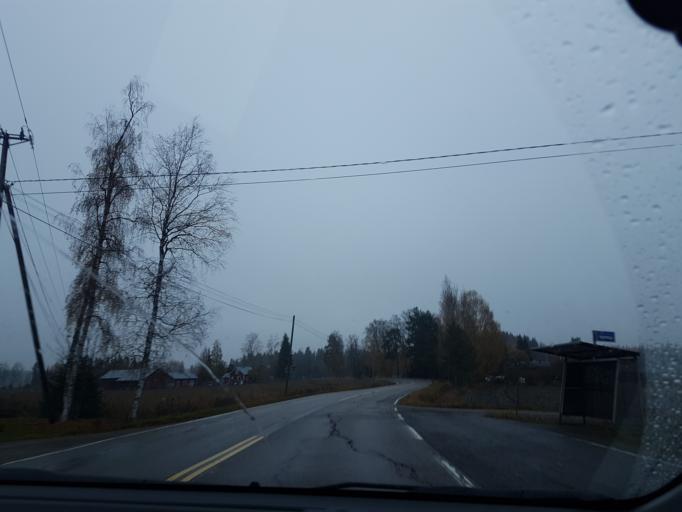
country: FI
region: Uusimaa
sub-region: Helsinki
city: Maentsaelae
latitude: 60.6022
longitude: 25.2036
